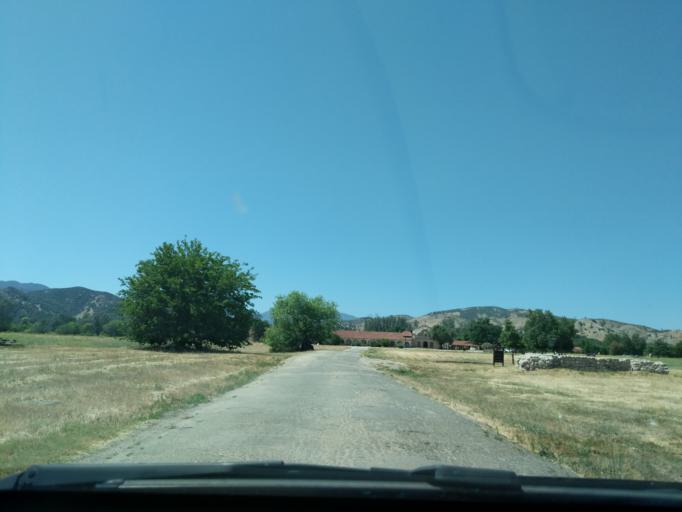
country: US
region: California
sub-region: Monterey County
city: King City
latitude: 36.0132
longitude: -121.2481
